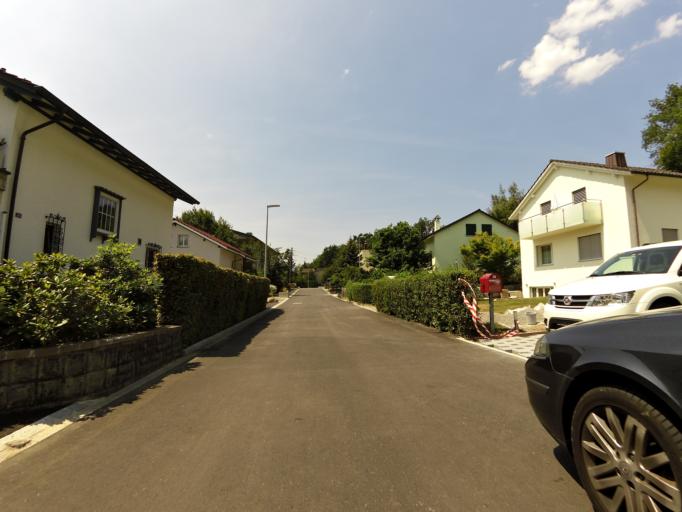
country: CH
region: Aargau
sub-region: Bezirk Baden
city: Killwangen
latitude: 47.4364
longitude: 8.3526
